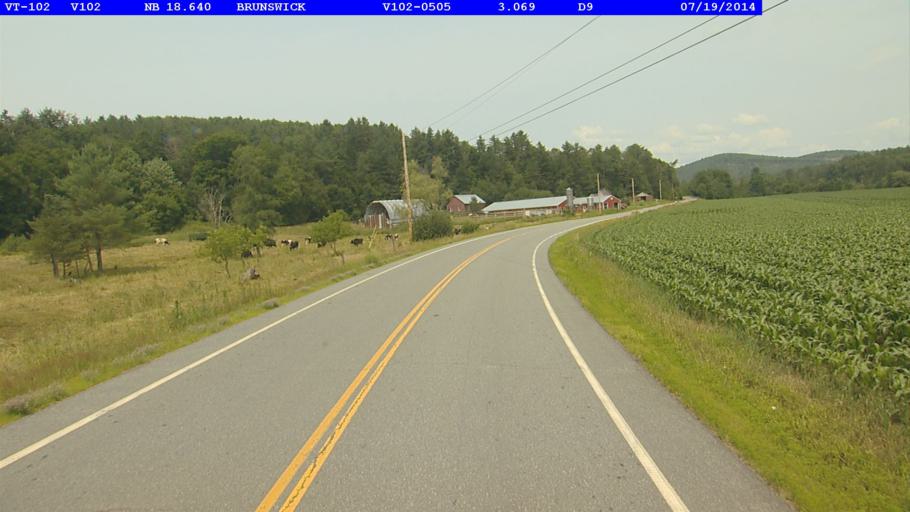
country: US
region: New Hampshire
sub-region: Coos County
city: Stratford
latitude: 44.7028
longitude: -71.6052
